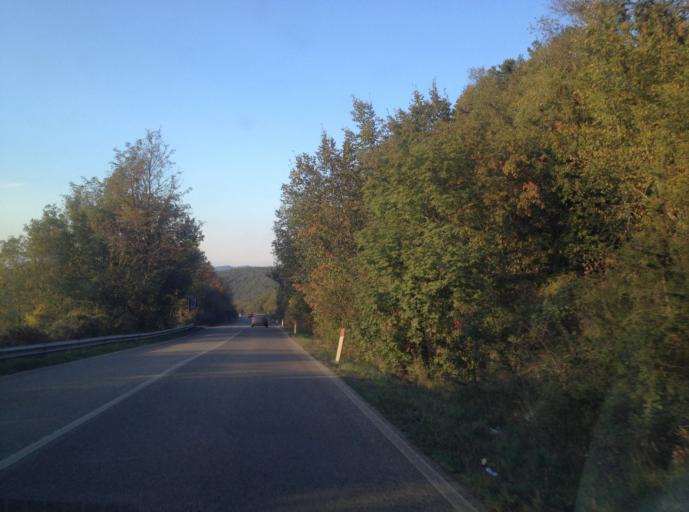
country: IT
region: Tuscany
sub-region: Provincia di Siena
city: Castellina in Chianti
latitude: 43.4937
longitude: 11.2999
